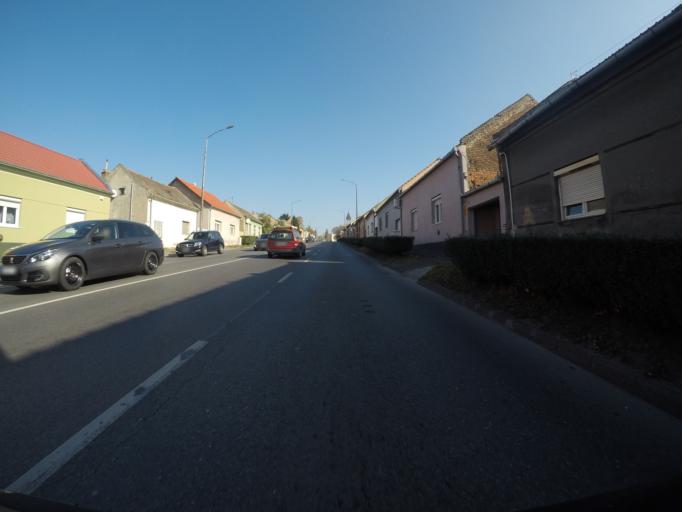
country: HU
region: Baranya
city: Pecs
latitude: 46.0818
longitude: 18.2599
